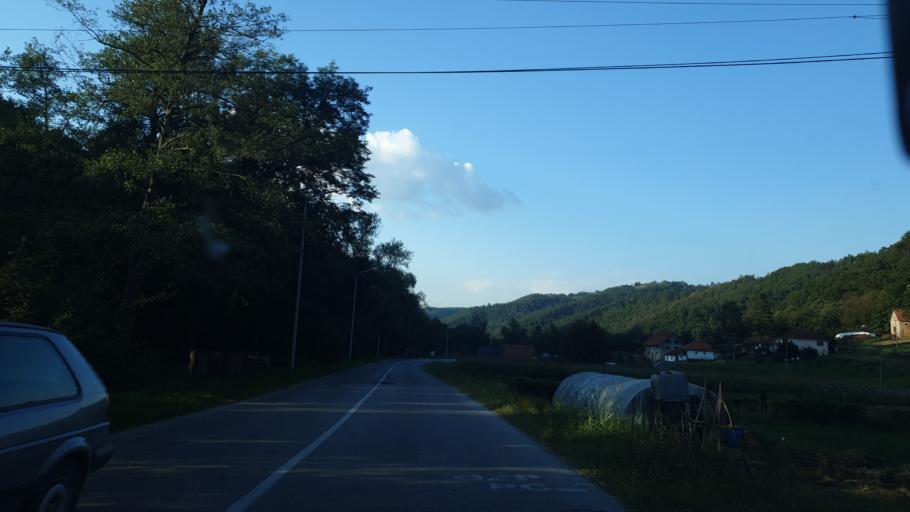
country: RS
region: Central Serbia
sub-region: Zlatiborski Okrug
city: Pozega
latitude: 43.9105
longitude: 20.0042
